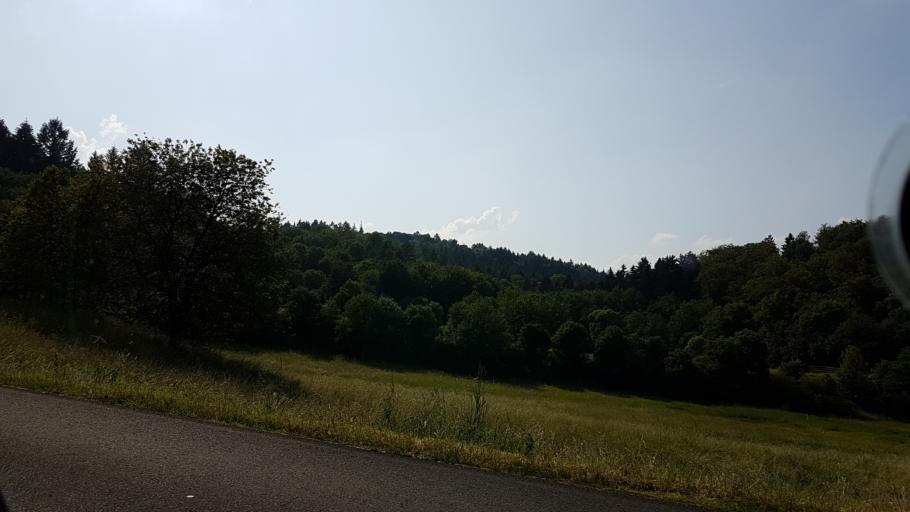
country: DE
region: Rheinland-Pfalz
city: Baumholder
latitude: 49.6209
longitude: 7.3528
